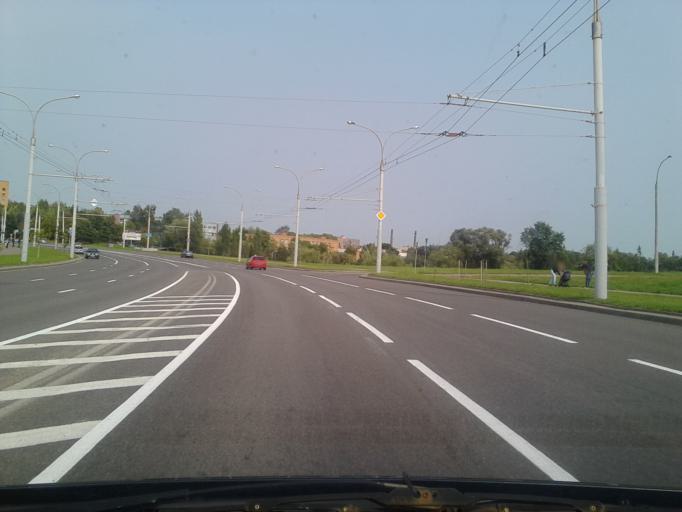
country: BY
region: Minsk
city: Yubilyeyny
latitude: 53.8556
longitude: 27.4973
